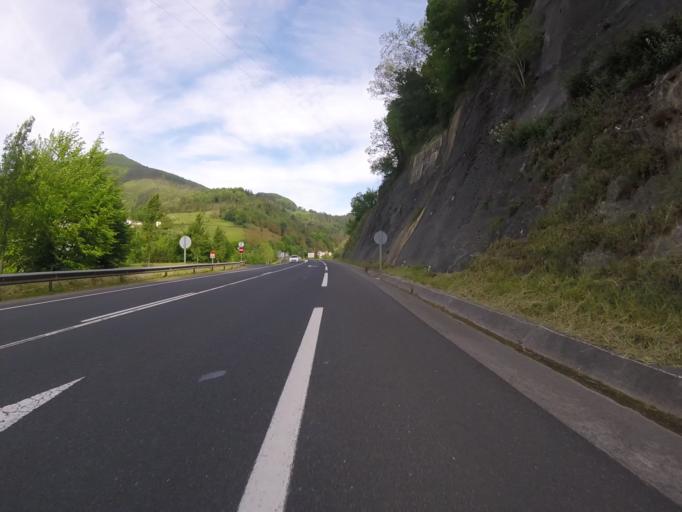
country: ES
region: Basque Country
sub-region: Provincia de Guipuzcoa
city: Urretxu
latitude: 43.0974
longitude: -2.3150
